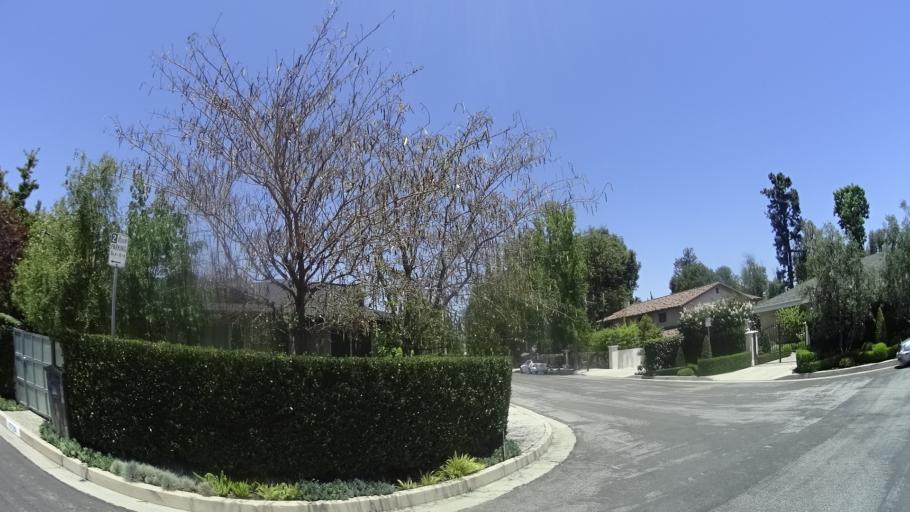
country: US
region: California
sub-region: Los Angeles County
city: Sherman Oaks
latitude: 34.1516
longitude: -118.4758
